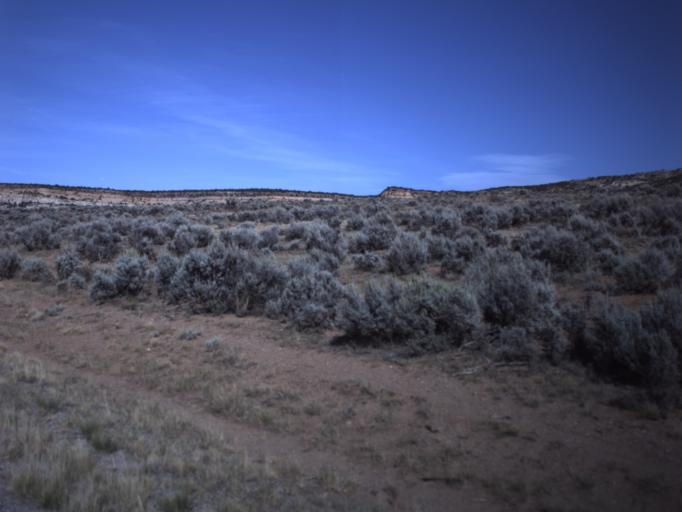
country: US
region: Utah
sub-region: San Juan County
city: Monticello
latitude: 38.0197
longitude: -109.4287
